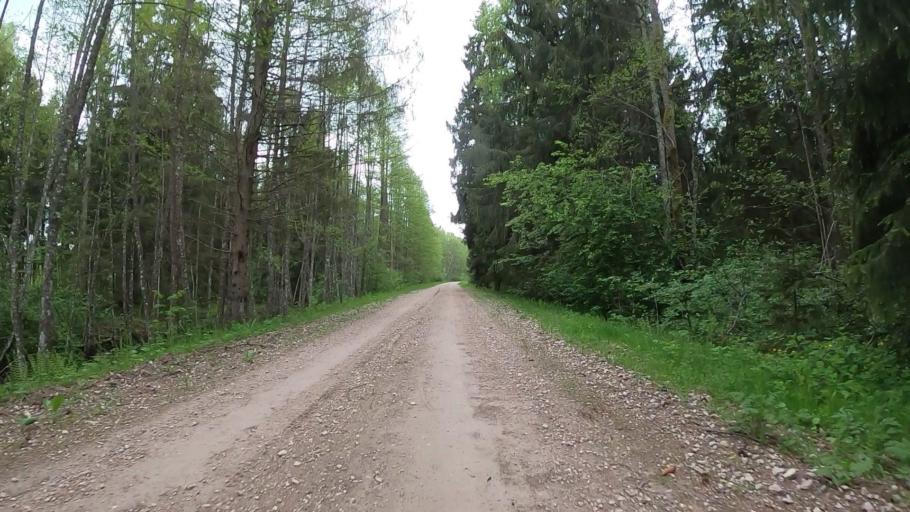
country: LV
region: Ozolnieku
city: Ozolnieki
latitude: 56.8022
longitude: 23.7845
